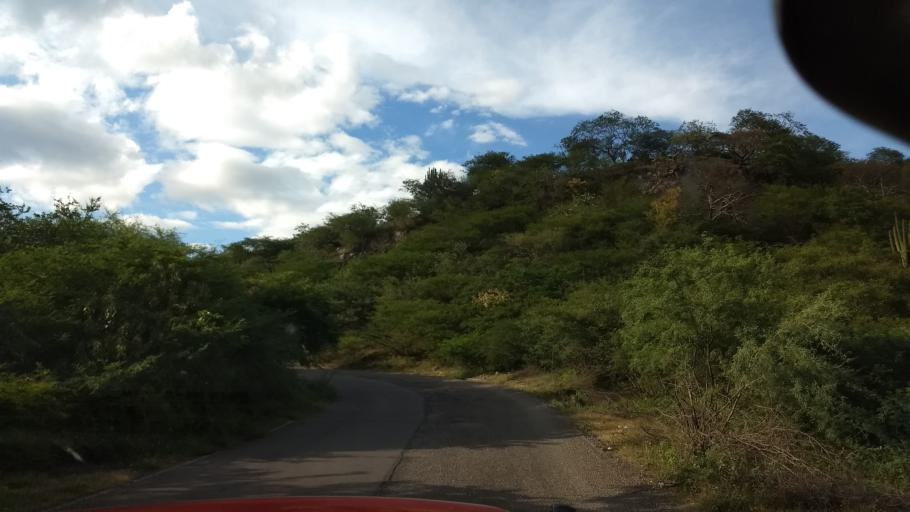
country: MX
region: Colima
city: Suchitlan
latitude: 19.4634
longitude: -103.8249
